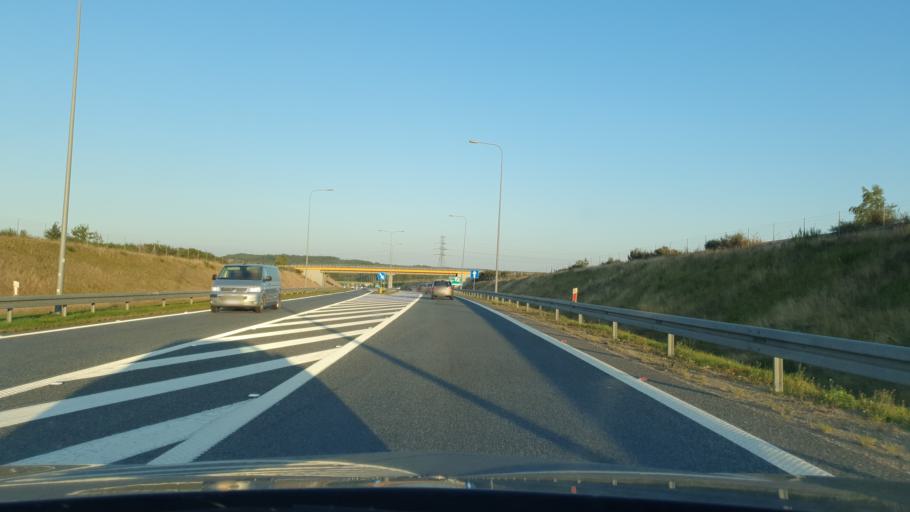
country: PL
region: Pomeranian Voivodeship
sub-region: Powiat slupski
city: Kobylnica
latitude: 54.4254
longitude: 16.9928
